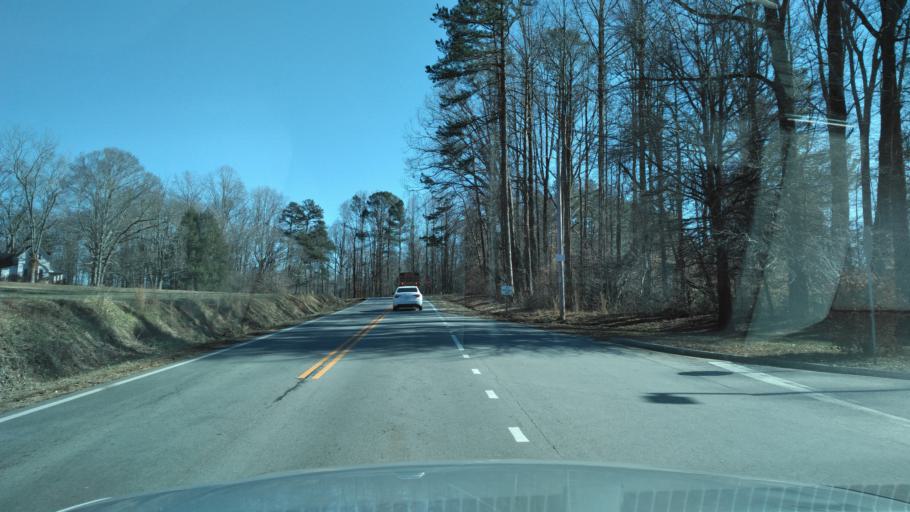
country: US
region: Georgia
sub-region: Hall County
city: Gainesville
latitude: 34.3104
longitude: -83.7416
